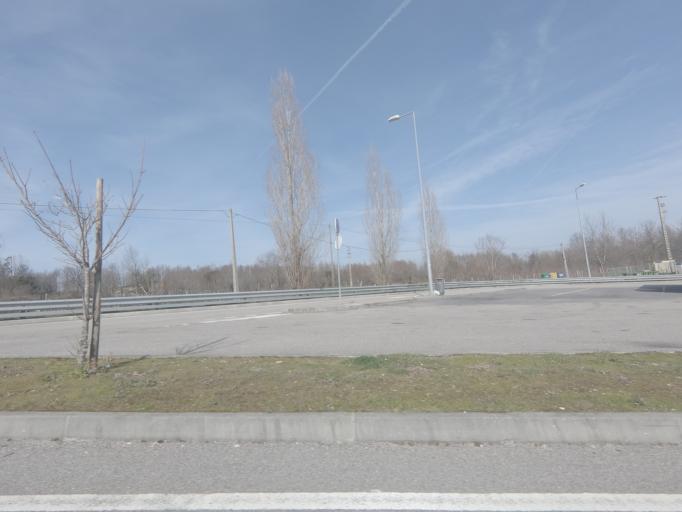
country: PT
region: Viseu
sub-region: Oliveira de Frades
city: Oliveira de Frades
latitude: 40.6872
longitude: -8.2320
